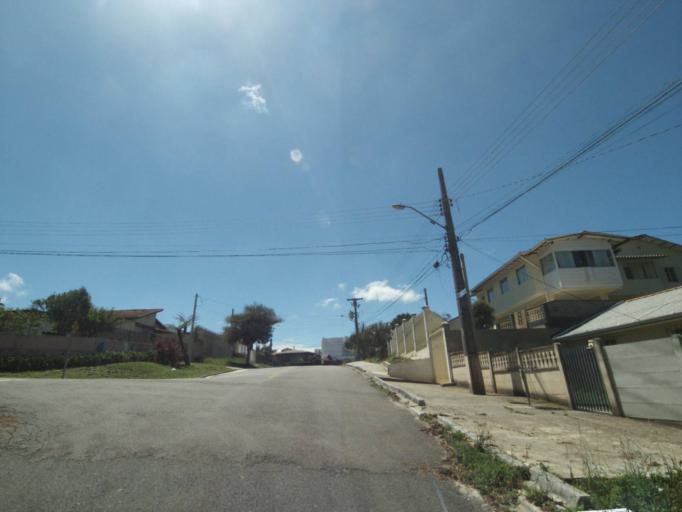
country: BR
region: Parana
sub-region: Curitiba
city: Curitiba
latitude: -25.3856
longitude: -49.2653
